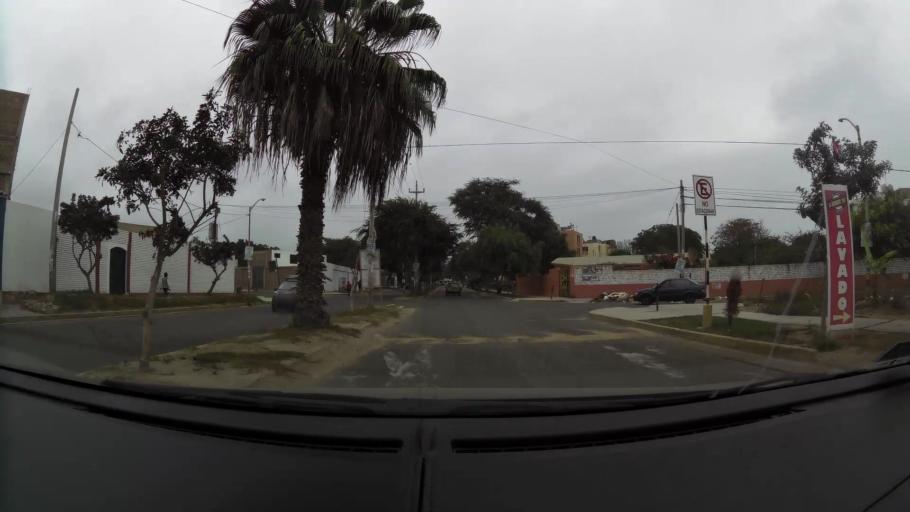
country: PE
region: La Libertad
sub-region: Provincia de Trujillo
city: Buenos Aires
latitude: -8.1247
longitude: -79.0425
